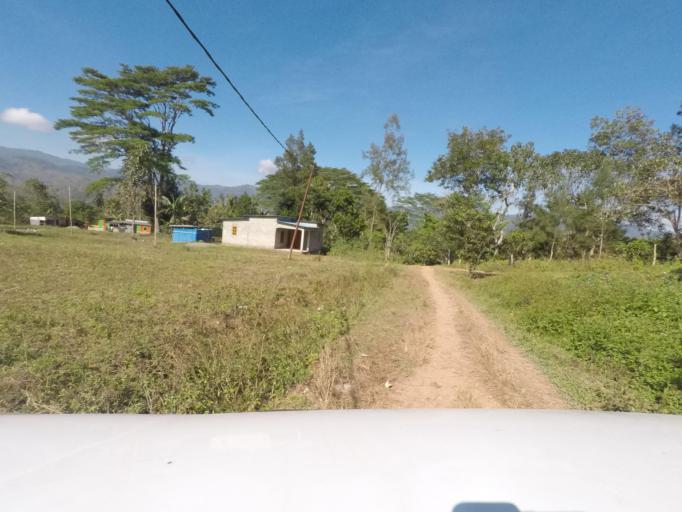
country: TL
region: Ermera
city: Gleno
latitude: -8.7086
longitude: 125.4490
